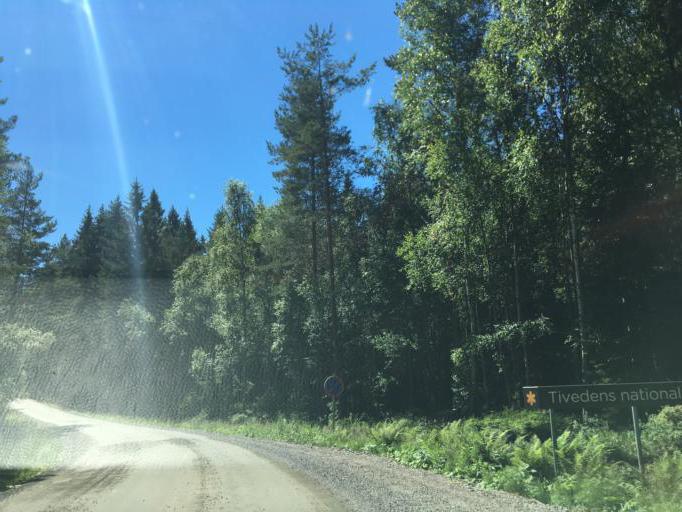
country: SE
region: Vaestra Goetaland
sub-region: Karlsborgs Kommun
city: Karlsborg
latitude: 58.7284
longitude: 14.5893
